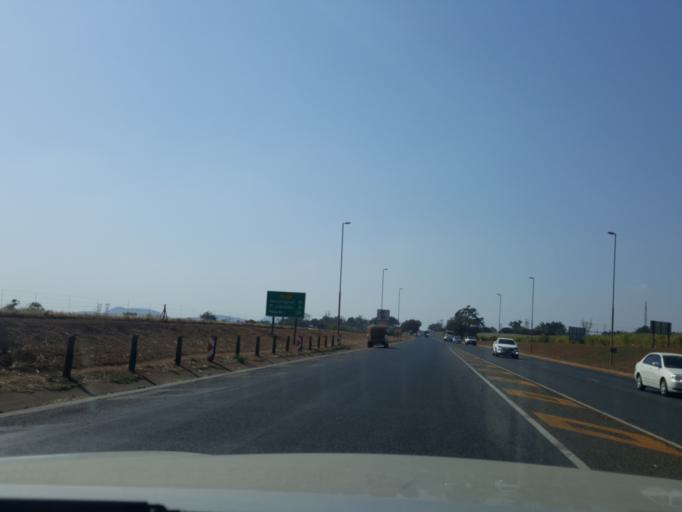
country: SZ
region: Hhohho
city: Ntfonjeni
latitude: -25.4960
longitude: 31.5166
